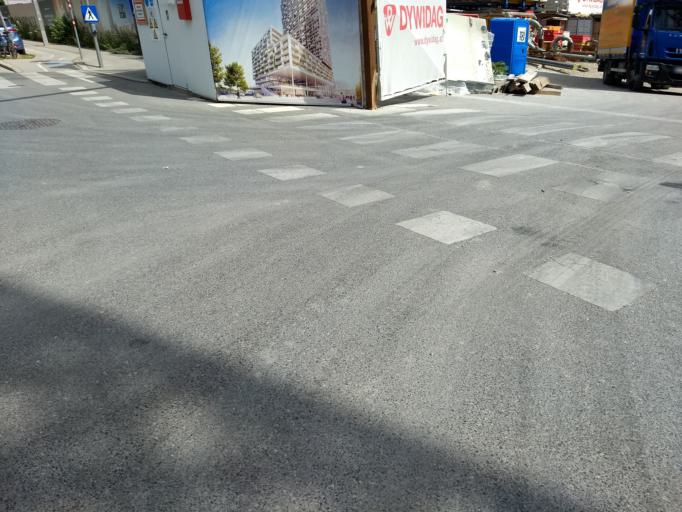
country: AT
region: Vienna
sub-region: Wien Stadt
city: Vienna
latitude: 48.2066
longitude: 16.4299
